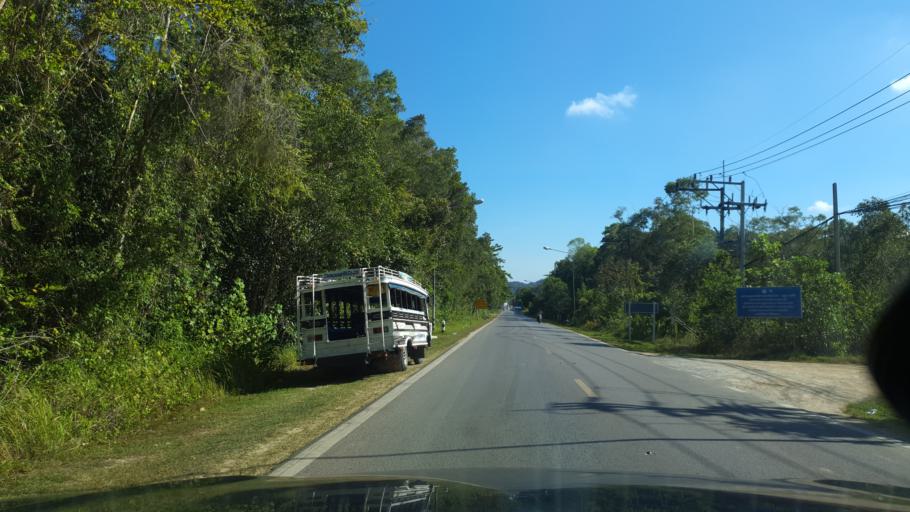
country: TH
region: Phangnga
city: Ban Ao Nang
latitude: 8.0482
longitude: 98.8026
